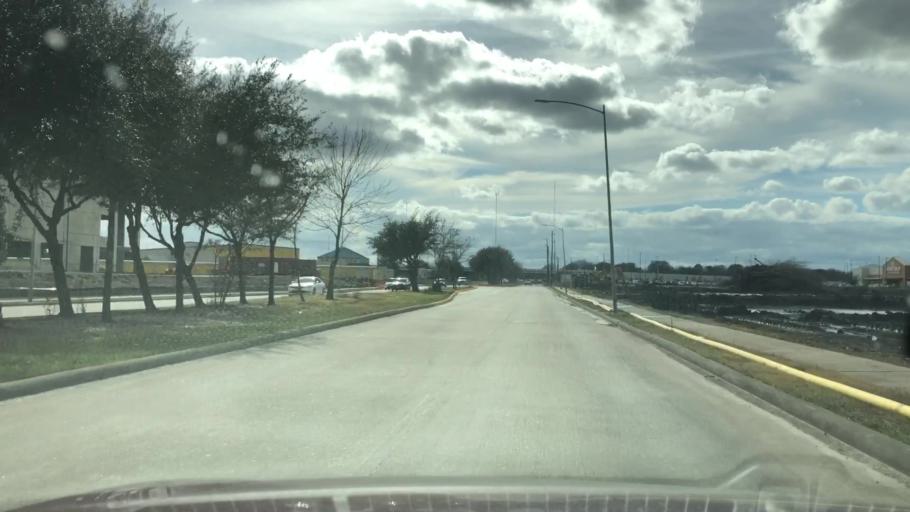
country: US
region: Texas
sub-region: Fort Bend County
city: Missouri City
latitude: 29.6092
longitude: -95.4733
